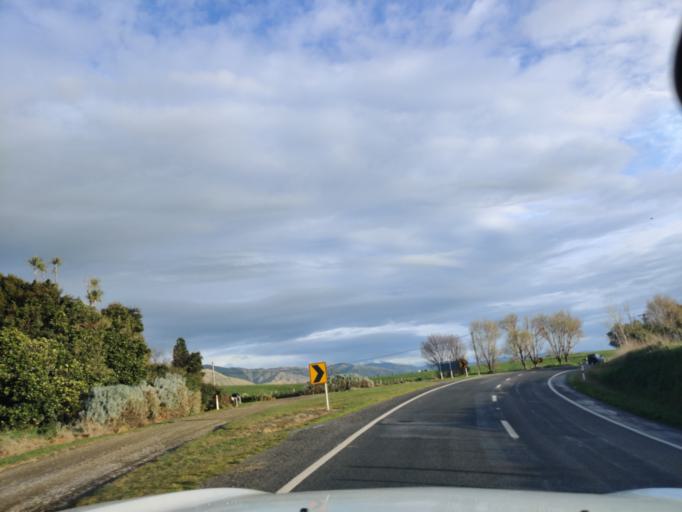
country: NZ
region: Manawatu-Wanganui
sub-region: Palmerston North City
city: Palmerston North
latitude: -40.4968
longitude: 175.4934
